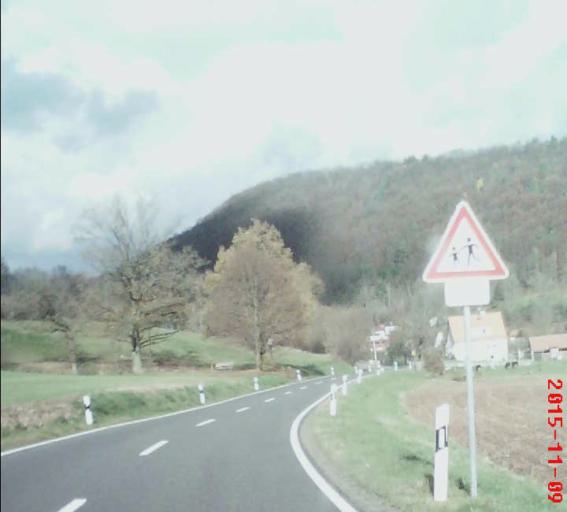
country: DE
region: Thuringia
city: Sickerode
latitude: 51.2480
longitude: 10.1250
